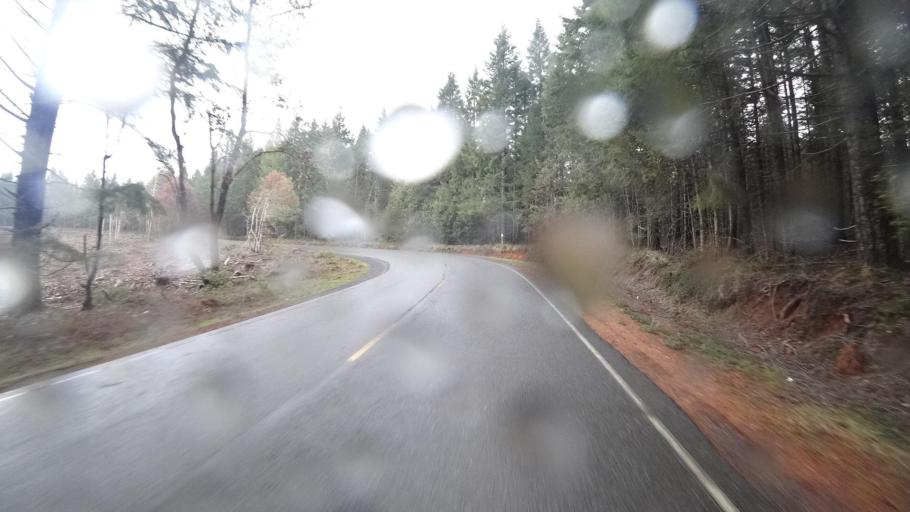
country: US
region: California
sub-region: Humboldt County
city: Willow Creek
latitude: 41.1761
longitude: -123.8158
